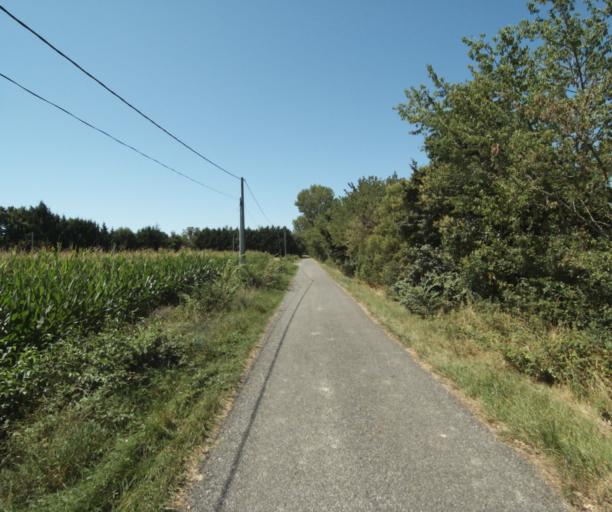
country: FR
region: Midi-Pyrenees
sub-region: Departement de la Haute-Garonne
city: Revel
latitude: 43.4898
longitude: 1.9580
